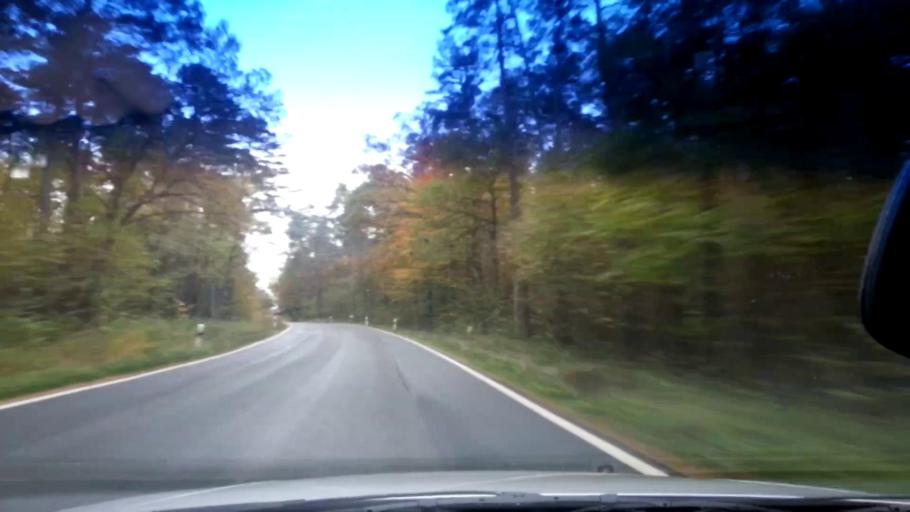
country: DE
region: Bavaria
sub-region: Upper Franconia
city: Burgebrach
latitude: 49.8110
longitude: 10.7845
